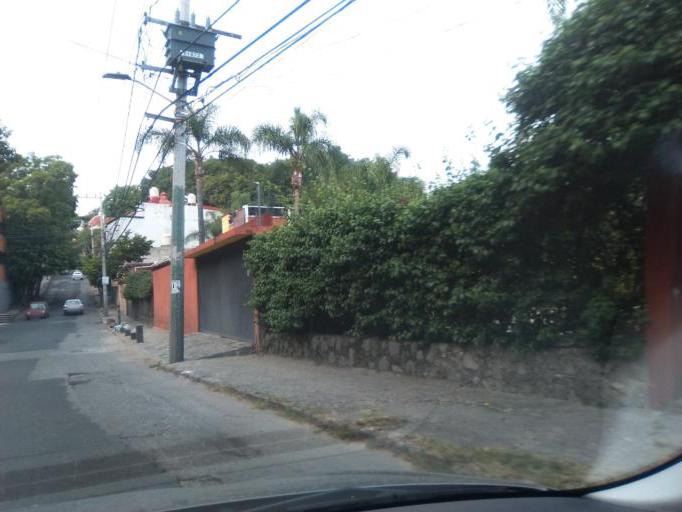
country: MX
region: Morelos
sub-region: Cuernavaca
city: Cuernavaca
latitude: 18.9115
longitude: -99.2292
